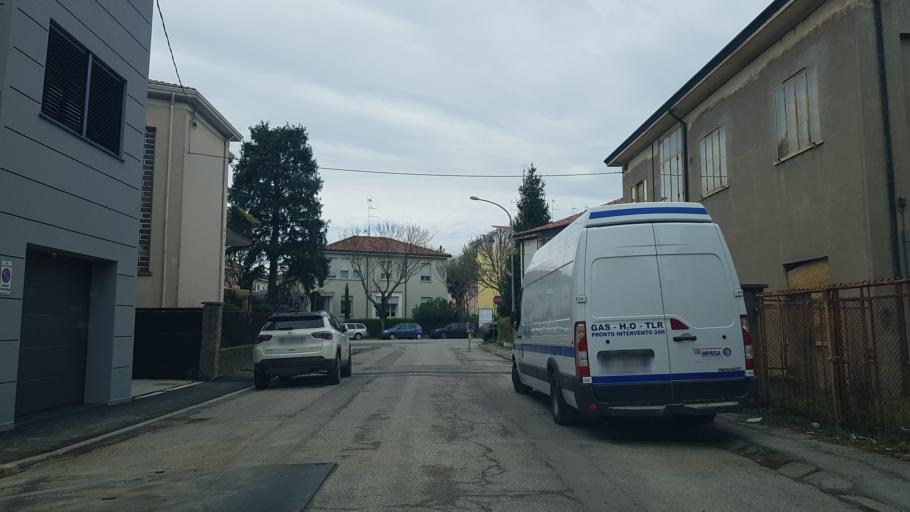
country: IT
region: Veneto
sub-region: Provincia di Rovigo
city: Rovigo
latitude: 45.0751
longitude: 11.7933
